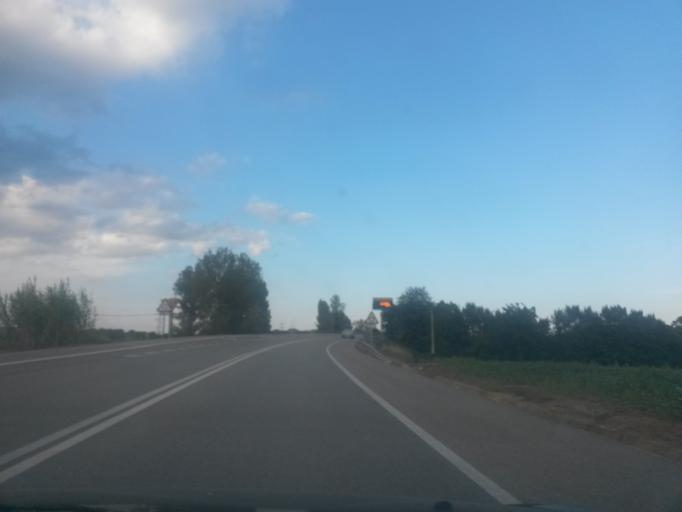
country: ES
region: Catalonia
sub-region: Provincia de Girona
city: Vilobi d'Onyar
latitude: 41.8900
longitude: 2.7731
